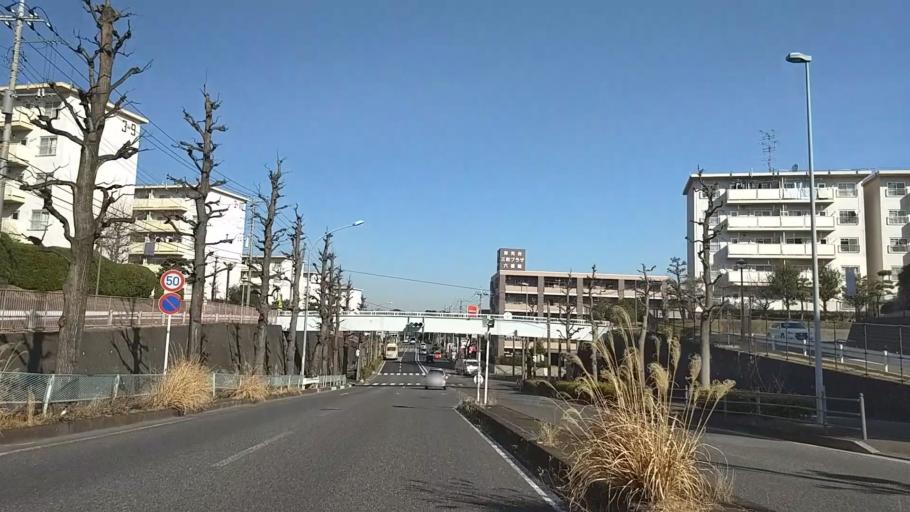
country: JP
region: Kanagawa
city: Yokohama
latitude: 35.3828
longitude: 139.5927
